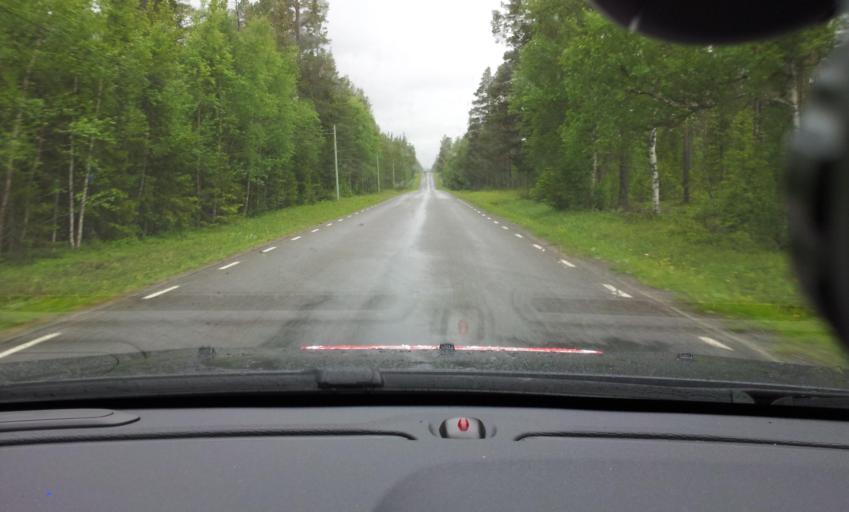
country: SE
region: Jaemtland
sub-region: Are Kommun
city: Are
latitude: 63.1801
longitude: 13.1105
